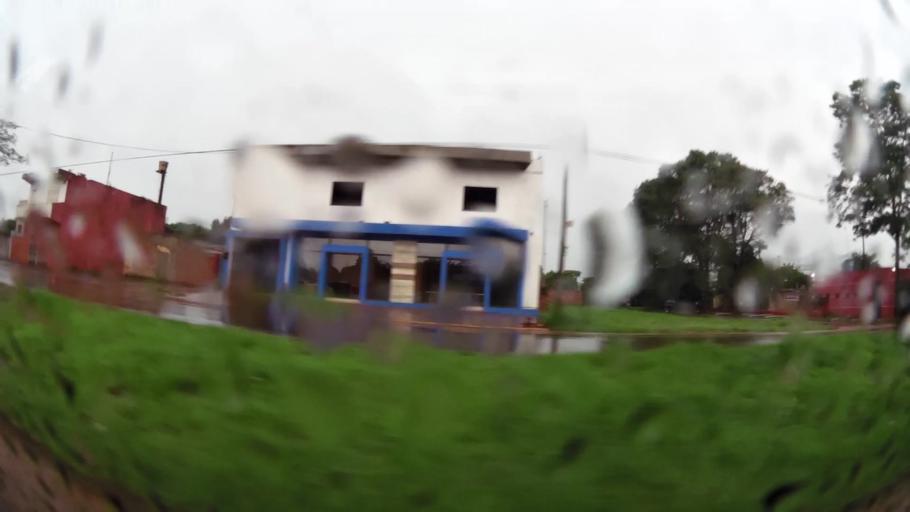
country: PY
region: Alto Parana
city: Presidente Franco
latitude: -25.5202
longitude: -54.6754
